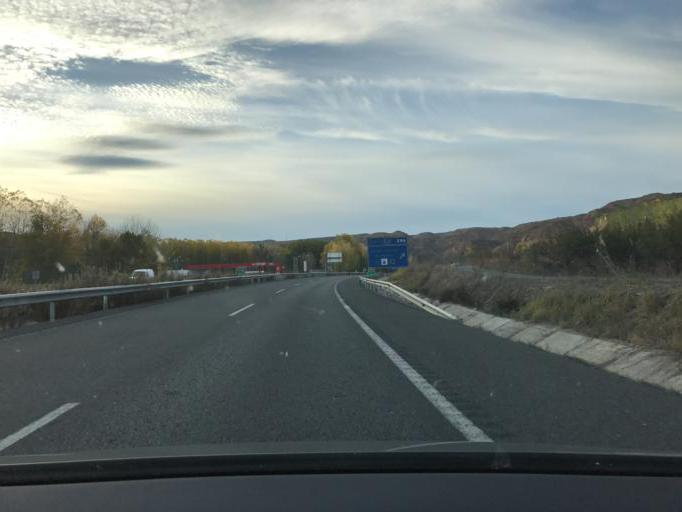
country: ES
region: Andalusia
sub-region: Provincia de Granada
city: Purullena
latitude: 37.3287
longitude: -3.2142
